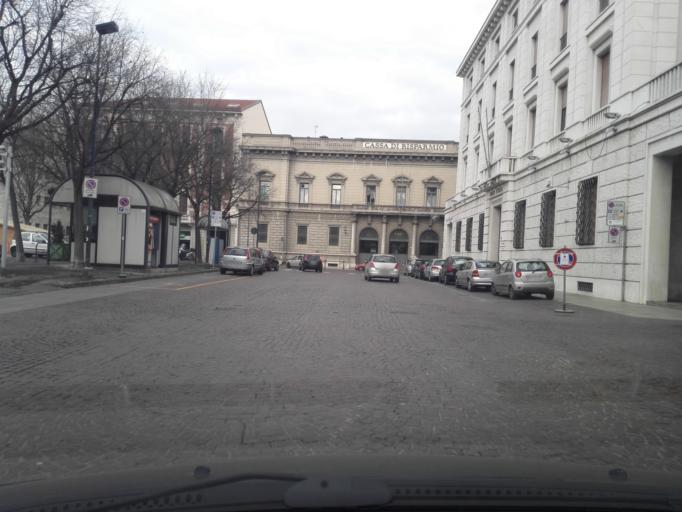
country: IT
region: Piedmont
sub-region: Provincia di Alessandria
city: Alessandria
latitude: 44.9131
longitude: 8.6169
